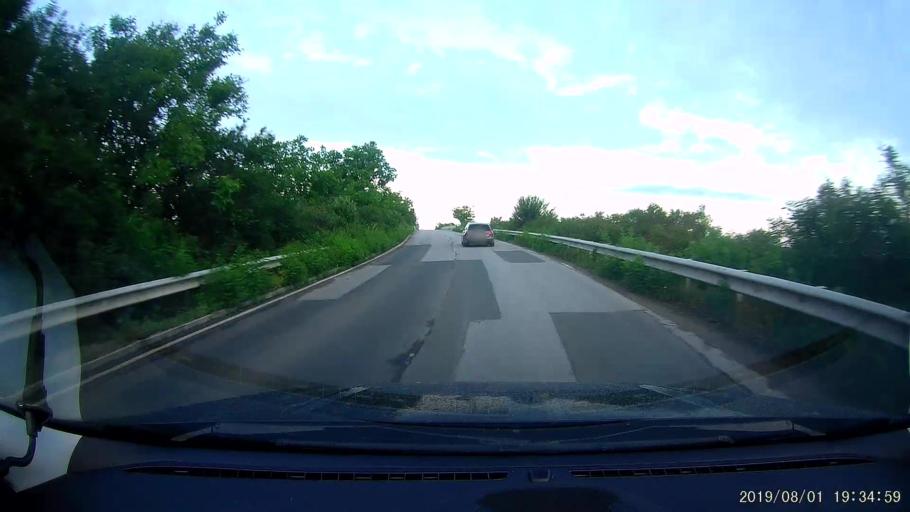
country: BG
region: Burgas
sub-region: Obshtina Sungurlare
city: Sungurlare
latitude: 42.7660
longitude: 26.8797
